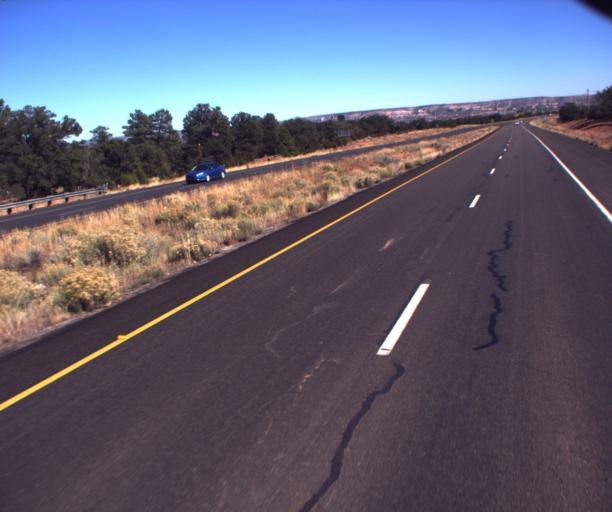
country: US
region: Arizona
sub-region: Apache County
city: Saint Michaels
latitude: 35.6589
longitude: -109.1274
